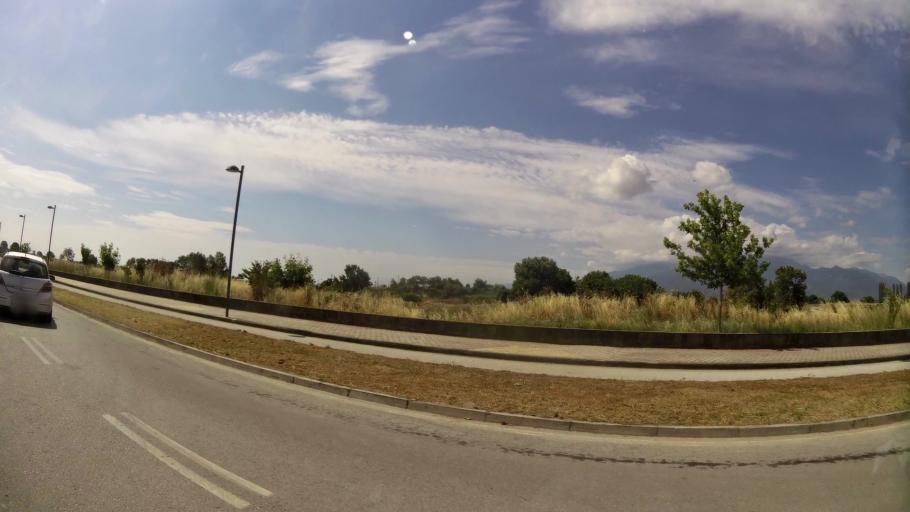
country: GR
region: Central Macedonia
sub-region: Nomos Pierias
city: Katerini
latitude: 40.2594
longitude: 22.4976
